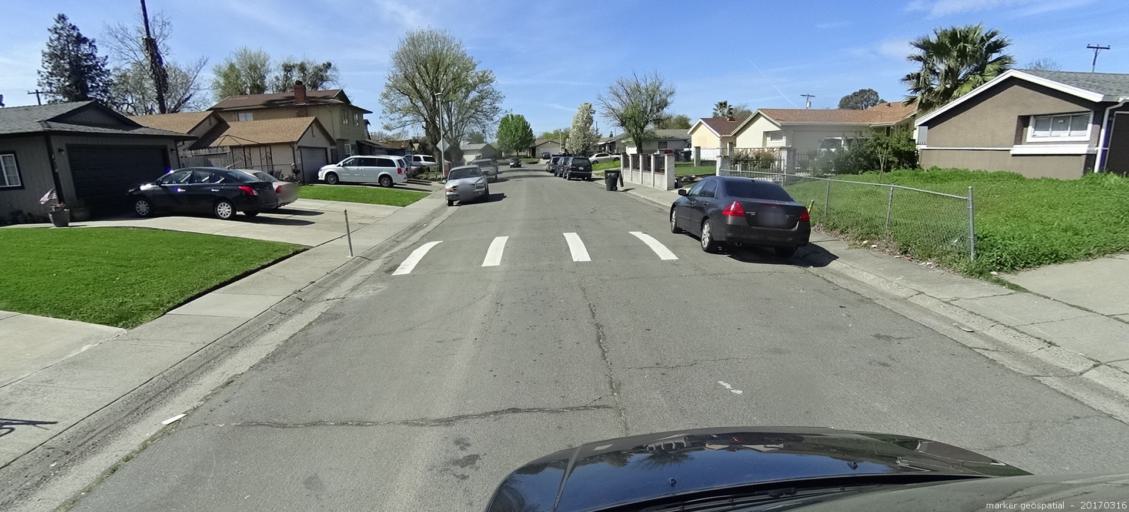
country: US
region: California
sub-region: Sacramento County
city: Parkway
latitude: 38.4780
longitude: -121.4846
